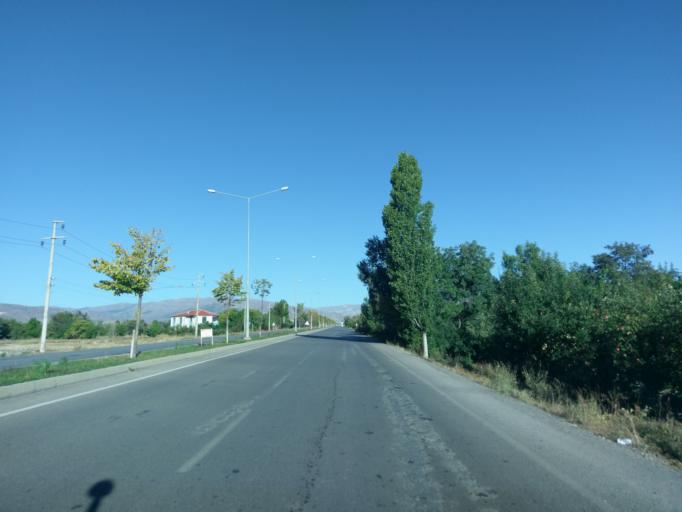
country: TR
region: Erzincan
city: Erzincan
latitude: 39.7731
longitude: 39.4216
